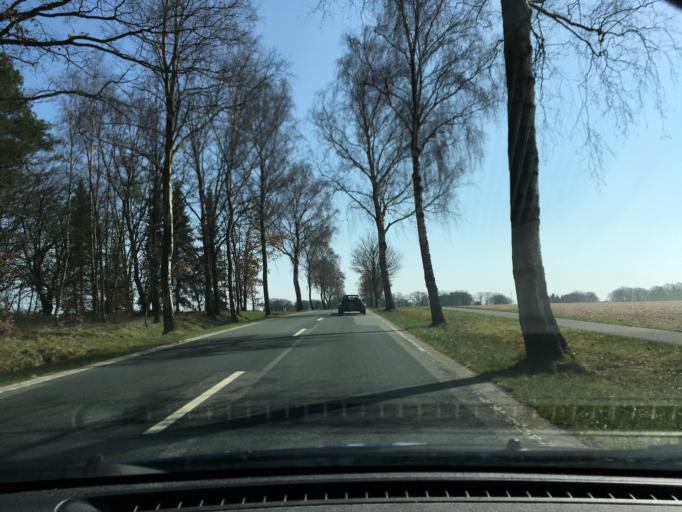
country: DE
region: Lower Saxony
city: Wriedel
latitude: 53.0595
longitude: 10.2886
